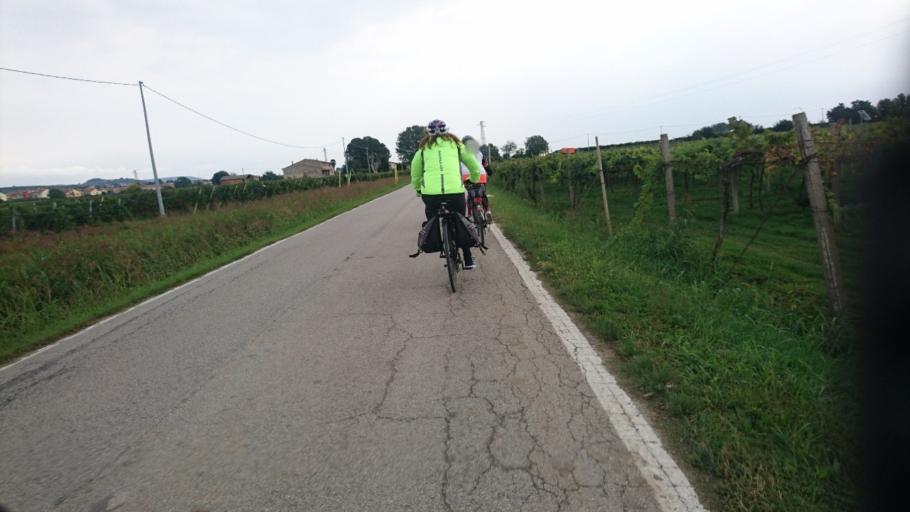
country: IT
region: Veneto
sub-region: Provincia di Verona
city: Caldierino-Rota
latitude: 45.4087
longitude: 11.1621
